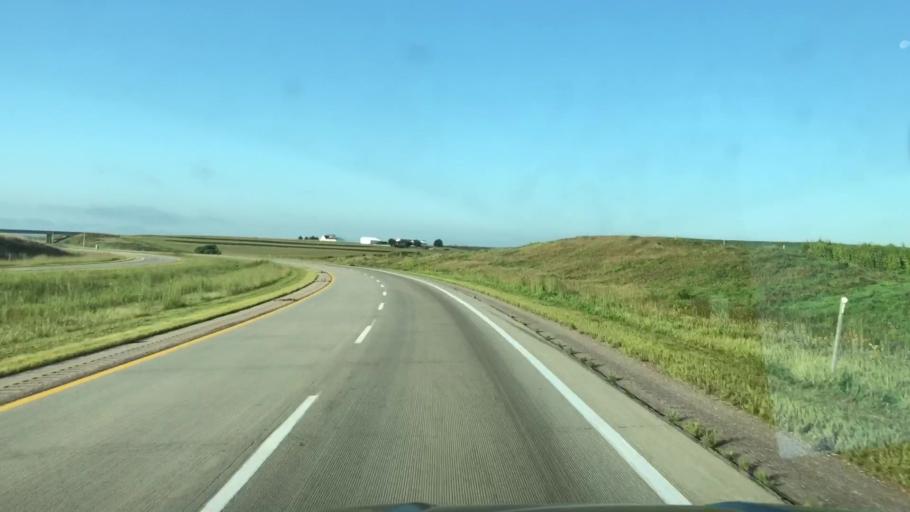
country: US
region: Iowa
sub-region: Sioux County
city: Alton
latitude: 42.9731
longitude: -96.0207
